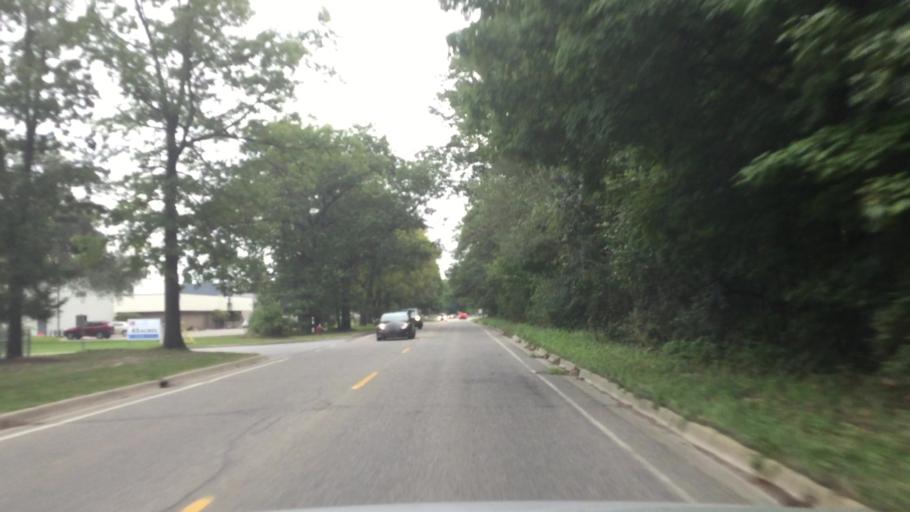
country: US
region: Michigan
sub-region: Livingston County
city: Brighton
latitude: 42.5004
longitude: -83.7625
